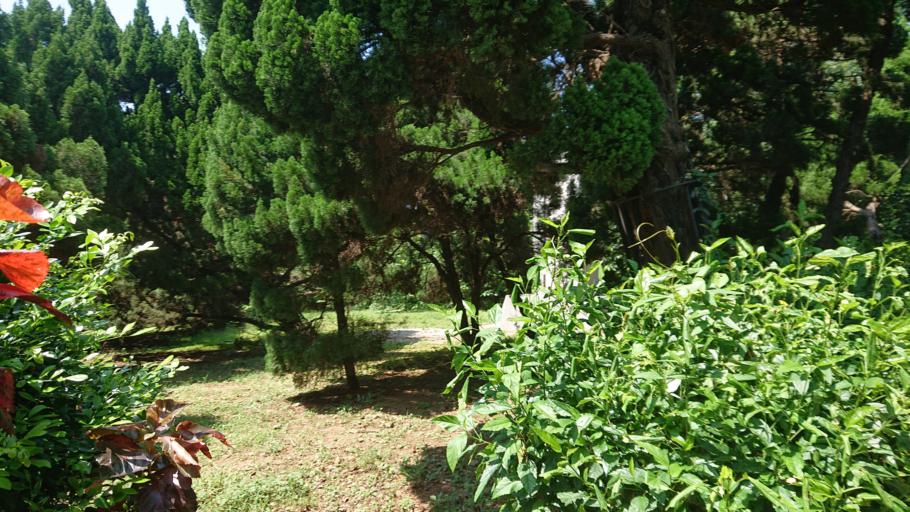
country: TW
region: Taiwan
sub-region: Hsinchu
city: Hsinchu
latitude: 24.7877
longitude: 120.9705
